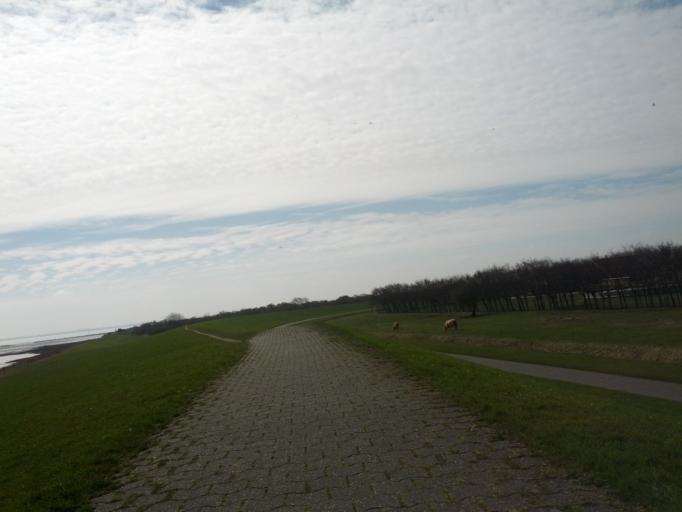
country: DE
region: Lower Saxony
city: Langeoog
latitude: 53.7343
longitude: 7.5013
